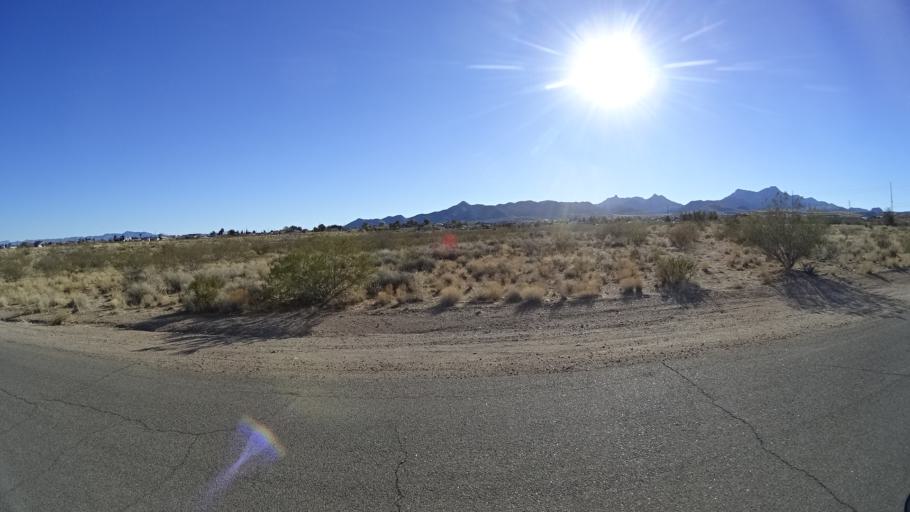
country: US
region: Arizona
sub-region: Mohave County
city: Kingman
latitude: 35.1831
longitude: -113.9983
